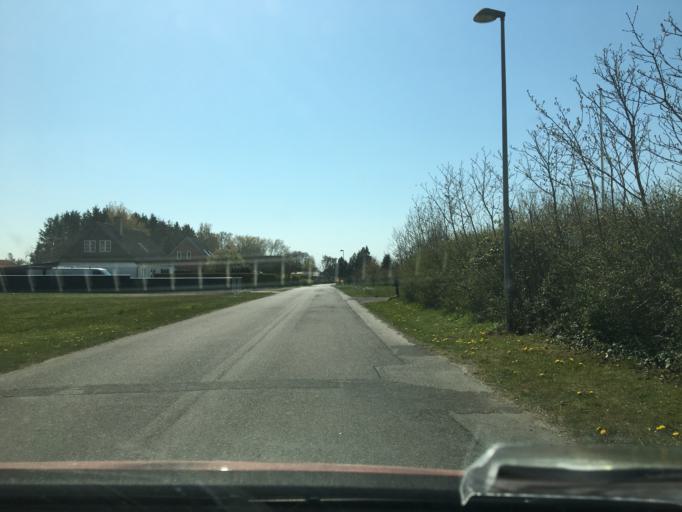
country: DK
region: Zealand
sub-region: Guldborgsund Kommune
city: Nykobing Falster
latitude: 54.7648
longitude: 11.7878
